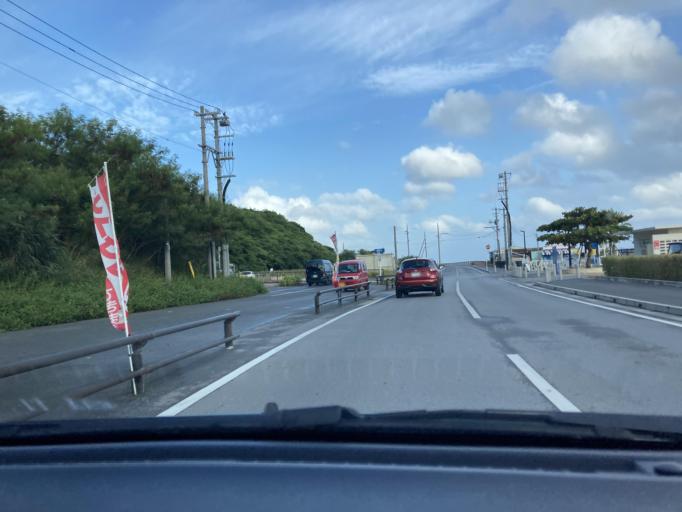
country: JP
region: Okinawa
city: Tomigusuku
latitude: 26.1753
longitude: 127.6440
